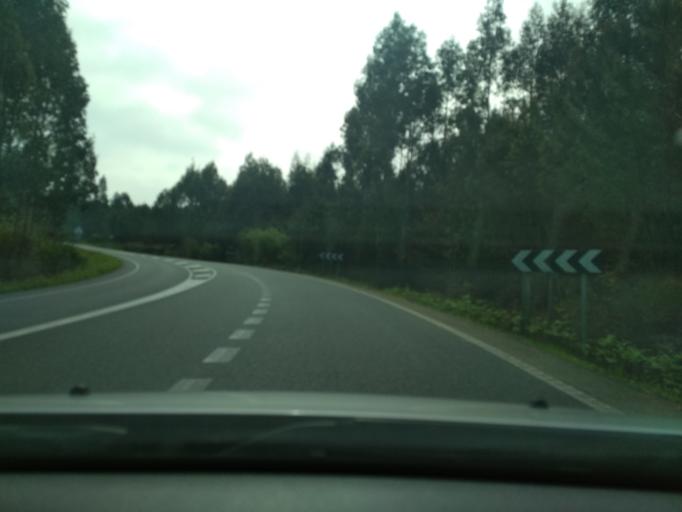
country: ES
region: Galicia
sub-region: Provincia de Pontevedra
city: Catoira
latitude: 42.6532
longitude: -8.7042
